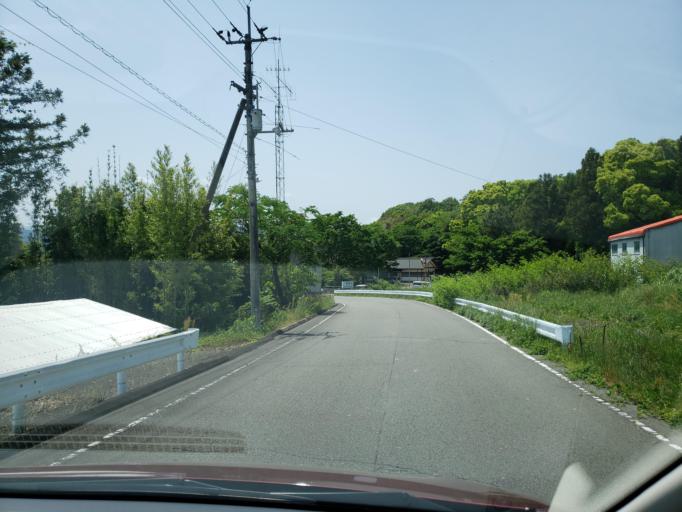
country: JP
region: Tokushima
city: Wakimachi
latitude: 34.0823
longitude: 134.2005
